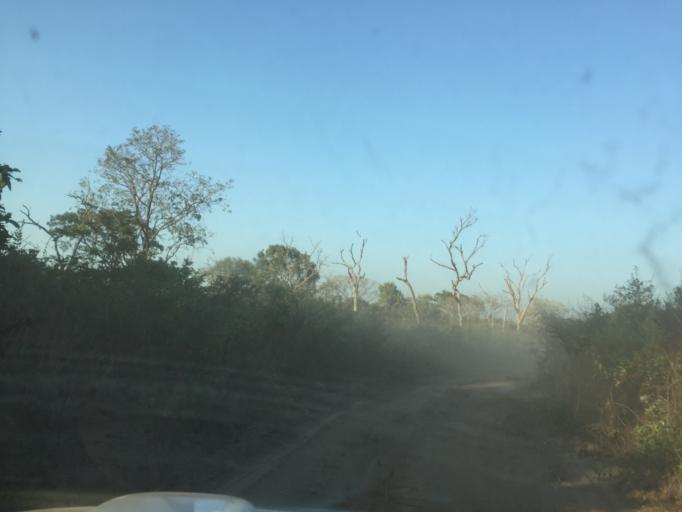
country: GW
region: Oio
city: Farim
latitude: 12.5302
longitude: -15.2760
